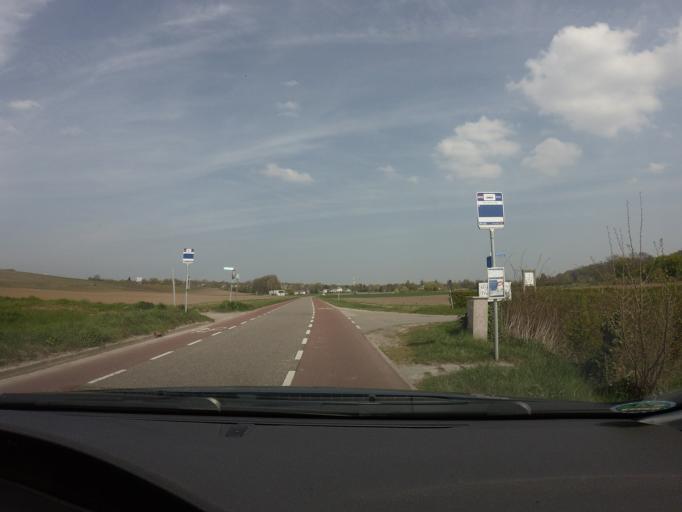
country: NL
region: Limburg
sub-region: Gemeente Maastricht
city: Maastricht
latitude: 50.8282
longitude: 5.6698
